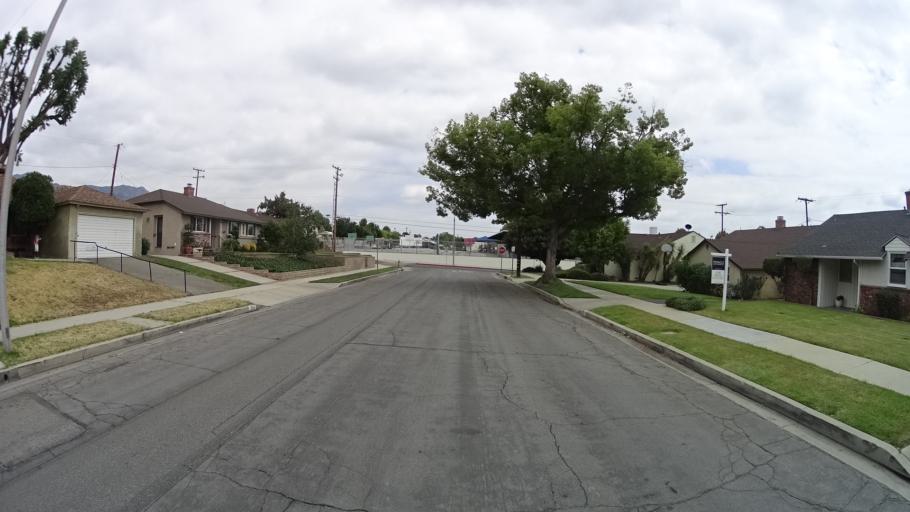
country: US
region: California
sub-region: Los Angeles County
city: Burbank
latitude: 34.2000
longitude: -118.3222
